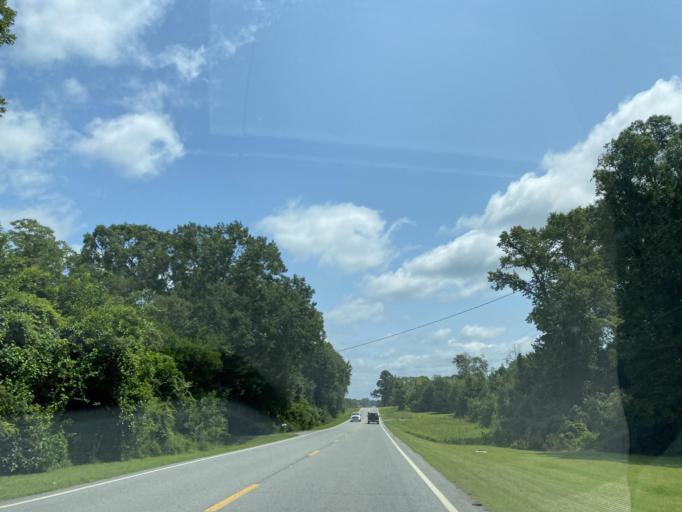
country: US
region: Georgia
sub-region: Telfair County
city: Helena
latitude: 32.0195
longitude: -83.0505
